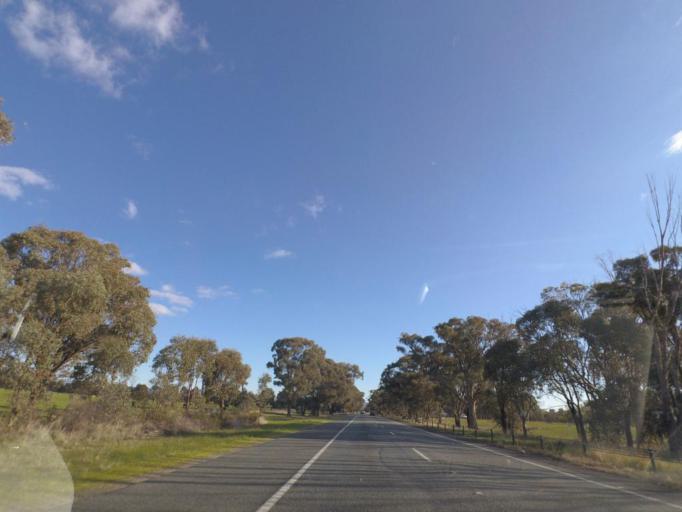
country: AU
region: Victoria
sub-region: Benalla
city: Benalla
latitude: -36.6911
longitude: 145.6620
